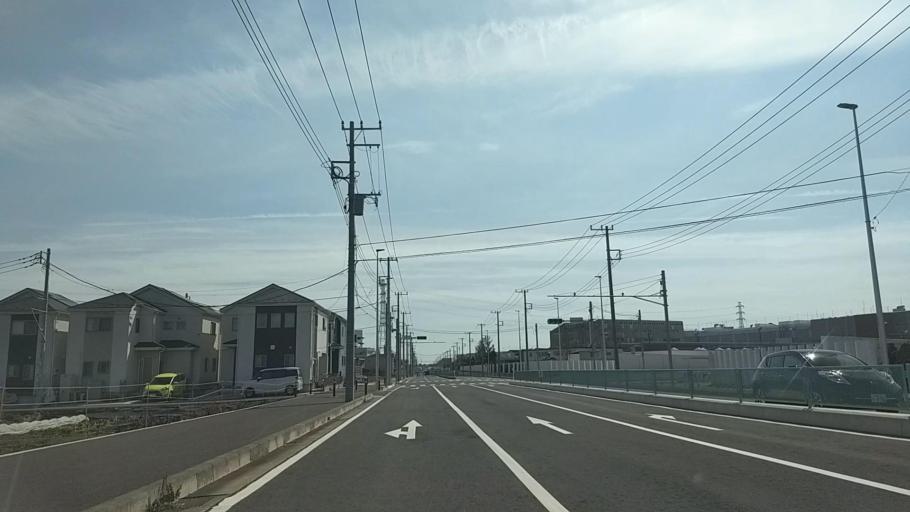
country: JP
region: Kanagawa
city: Fujisawa
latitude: 35.4033
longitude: 139.4550
